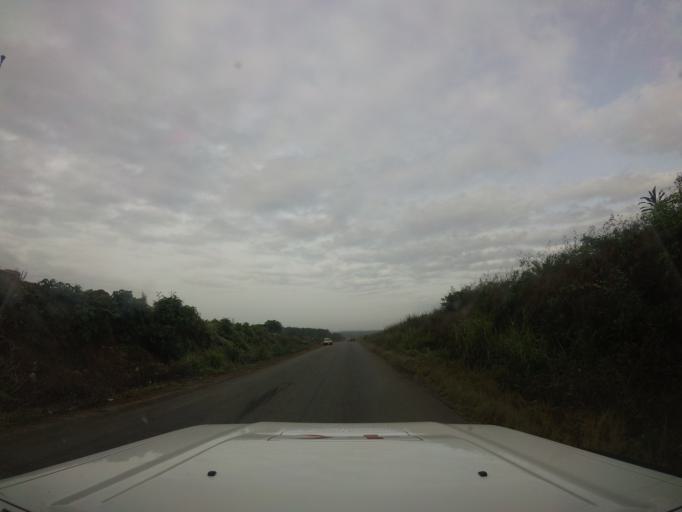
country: LR
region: Bomi
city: Tubmanburg
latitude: 6.7272
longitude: -11.0382
